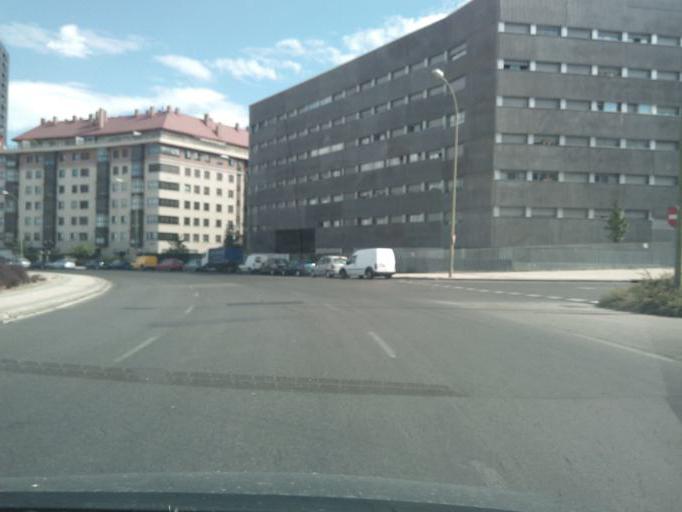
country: ES
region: Madrid
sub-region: Provincia de Madrid
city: Pinar de Chamartin
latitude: 40.4883
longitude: -3.6573
